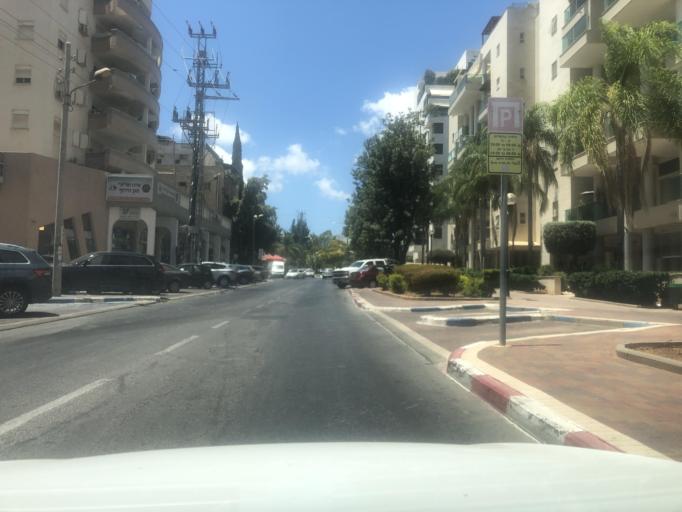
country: IL
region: Central District
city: Hod HaSharon
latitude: 32.1597
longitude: 34.9057
